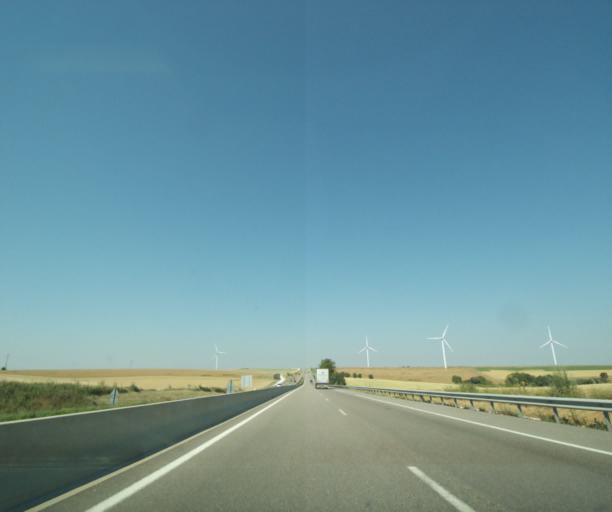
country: FR
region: Lorraine
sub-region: Departement de la Meuse
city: Ligny-en-Barrois
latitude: 48.7044
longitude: 5.4308
